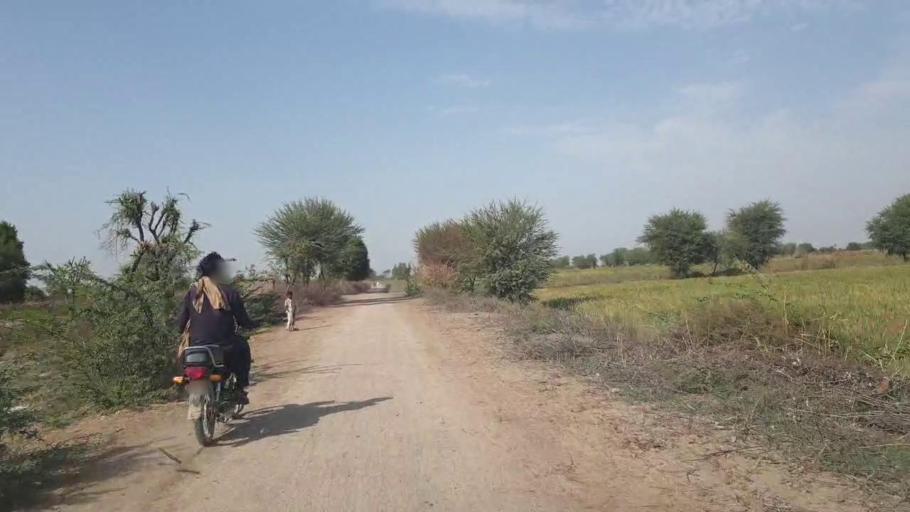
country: PK
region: Sindh
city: Dhoro Naro
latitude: 25.4441
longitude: 69.5490
